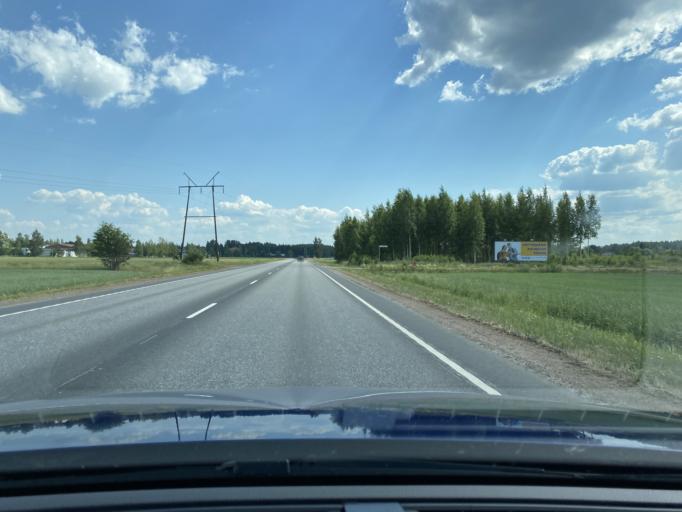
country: FI
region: Satakunta
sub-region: Rauma
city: Eura
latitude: 61.1419
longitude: 22.1118
